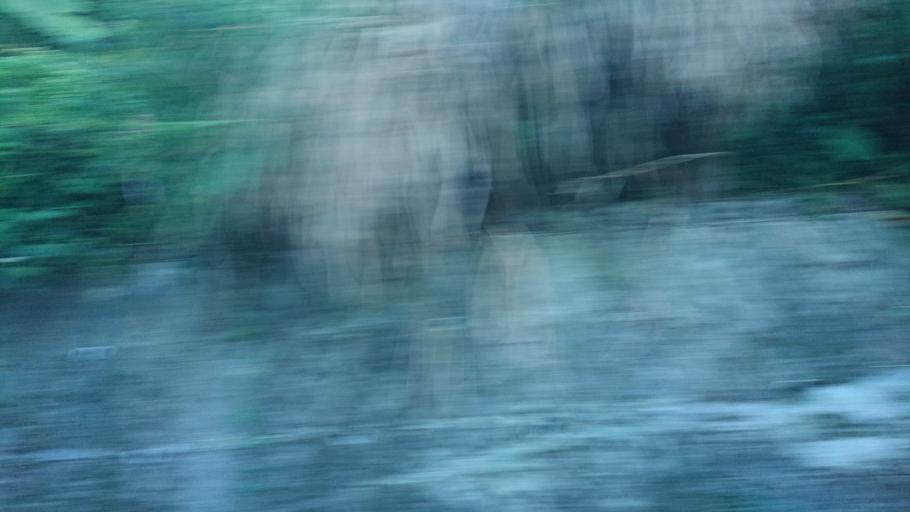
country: TW
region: Taiwan
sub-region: Chiayi
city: Jiayi Shi
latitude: 23.5254
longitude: 120.6322
